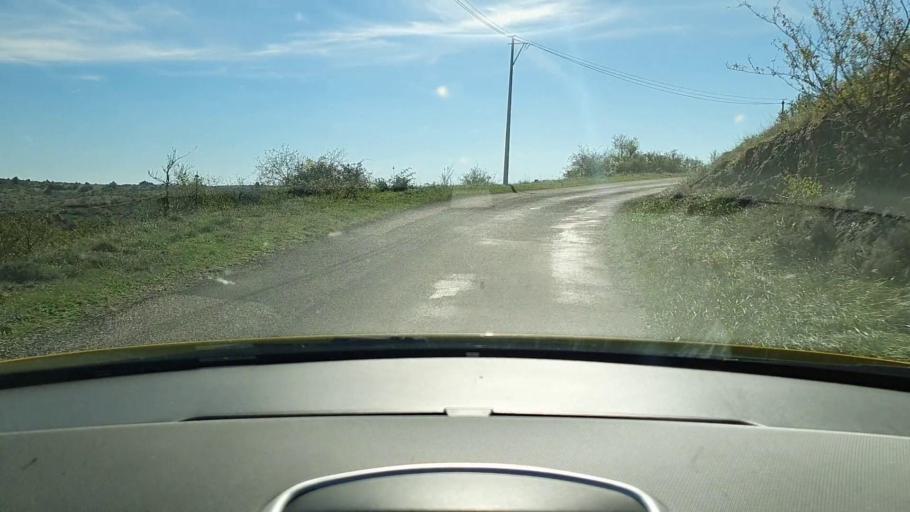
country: FR
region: Languedoc-Roussillon
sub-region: Departement du Gard
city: Le Vigan
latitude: 43.9611
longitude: 3.3921
